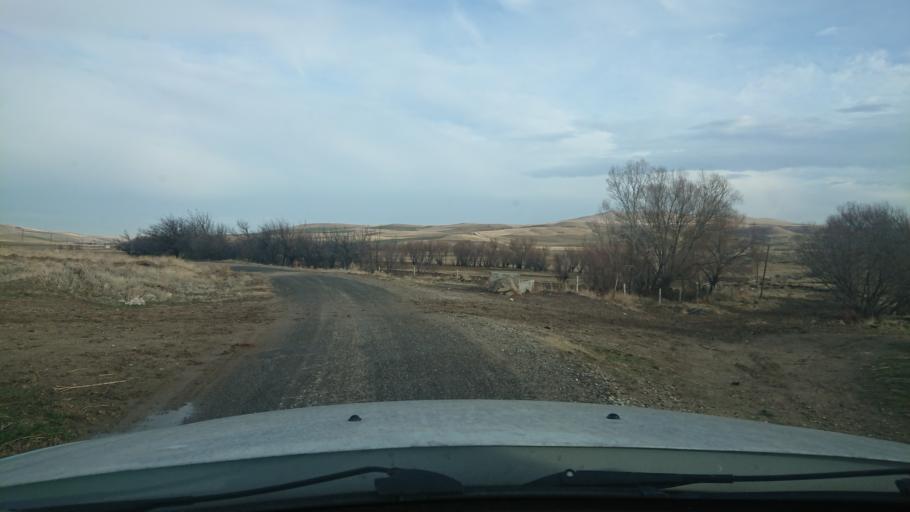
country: TR
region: Aksaray
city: Acipinar
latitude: 38.6775
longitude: 33.8670
